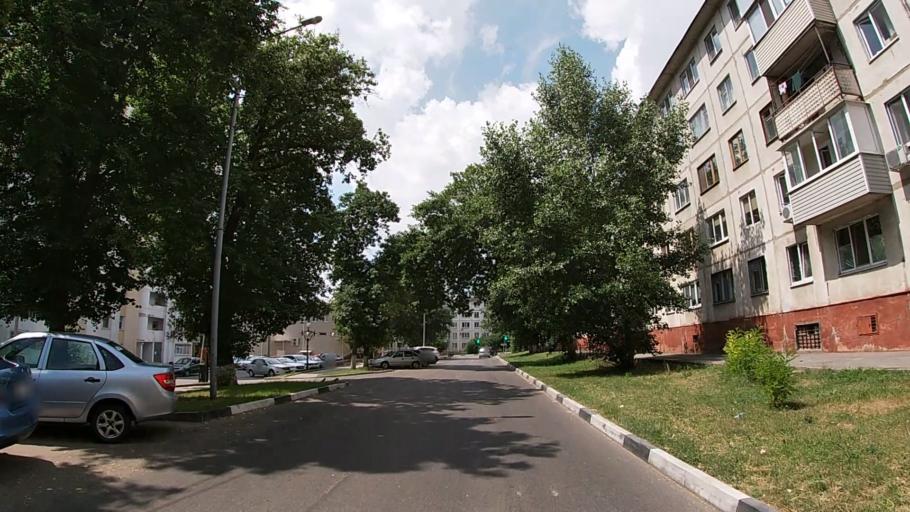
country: RU
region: Belgorod
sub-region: Belgorodskiy Rayon
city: Belgorod
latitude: 50.6045
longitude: 36.5971
